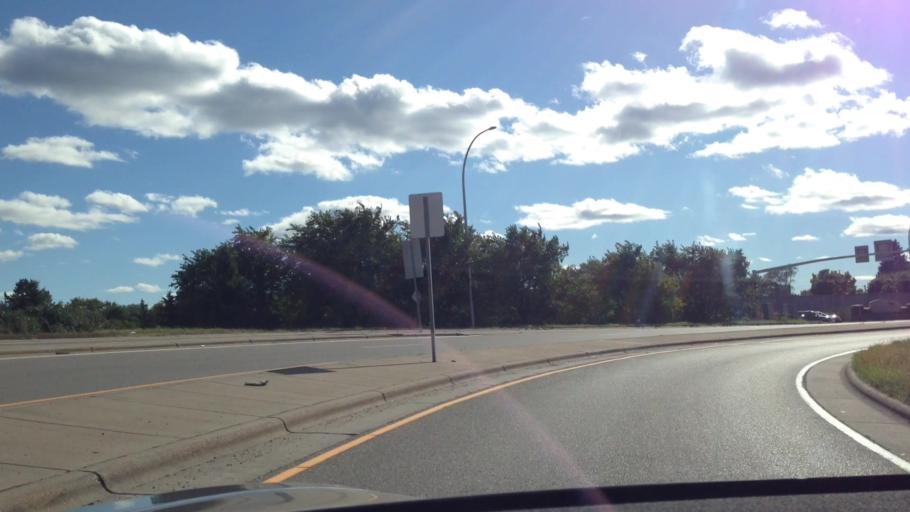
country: US
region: Minnesota
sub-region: Hennepin County
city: Robbinsdale
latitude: 45.0360
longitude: -93.3410
